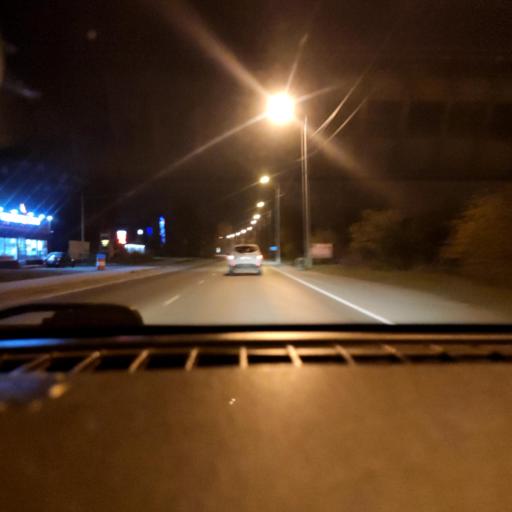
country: RU
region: Perm
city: Kondratovo
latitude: 57.9743
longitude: 56.1287
